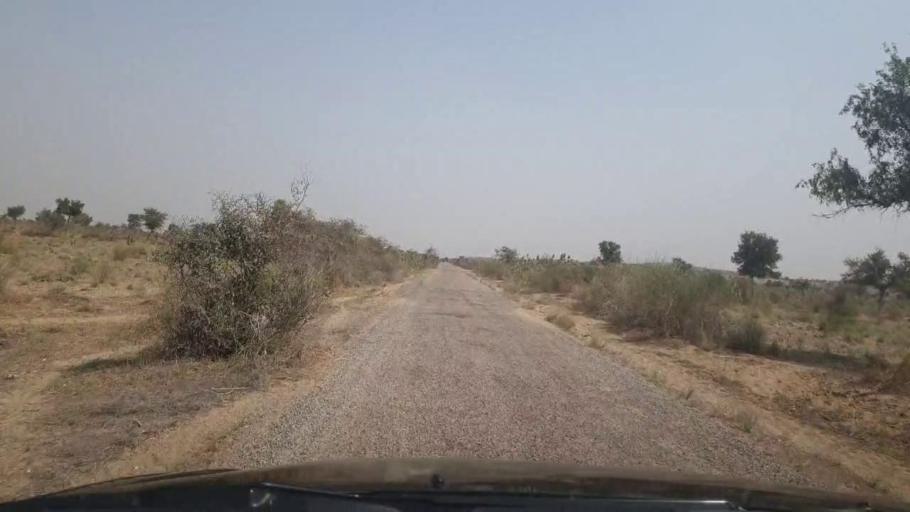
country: PK
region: Sindh
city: Islamkot
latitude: 25.0046
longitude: 70.3799
